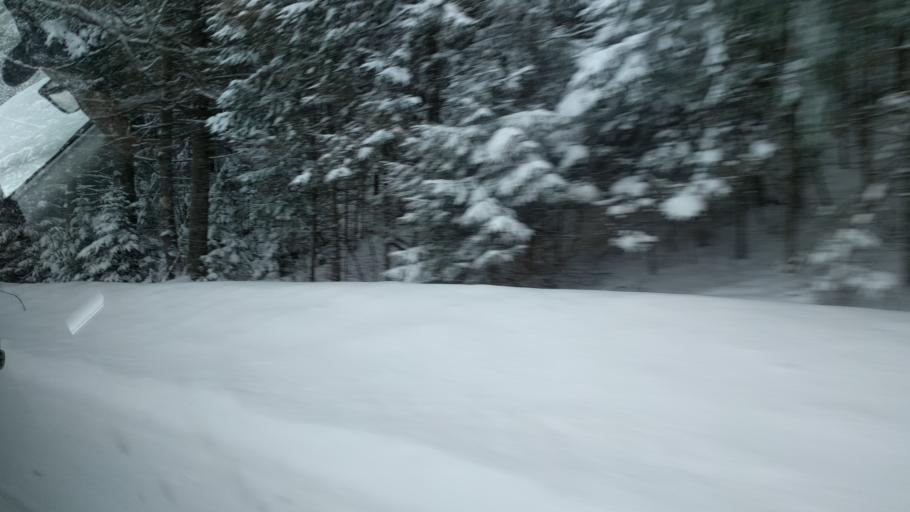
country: US
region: Wisconsin
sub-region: Iron County
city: Hurley
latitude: 46.4338
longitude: -90.2242
